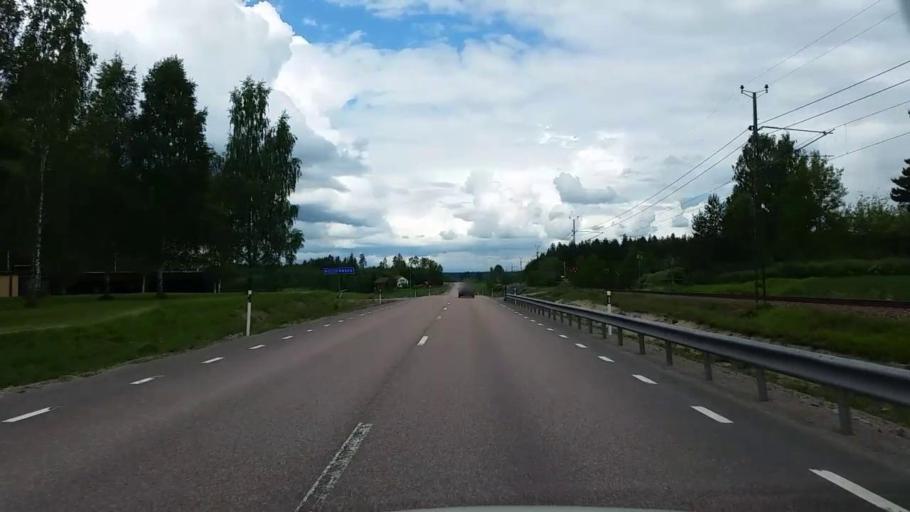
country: SE
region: Dalarna
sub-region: Avesta Kommun
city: Horndal
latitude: 60.3883
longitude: 16.4543
